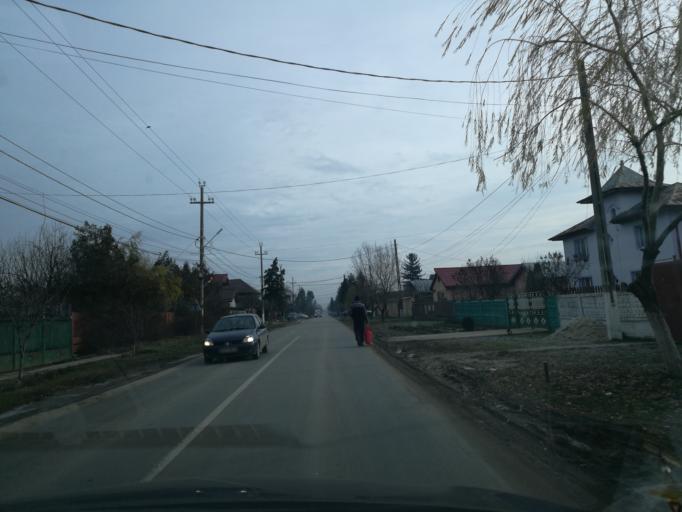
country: RO
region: Ilfov
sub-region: Comuna Moara Vlasiei
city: Caciulati
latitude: 44.6281
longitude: 26.1612
